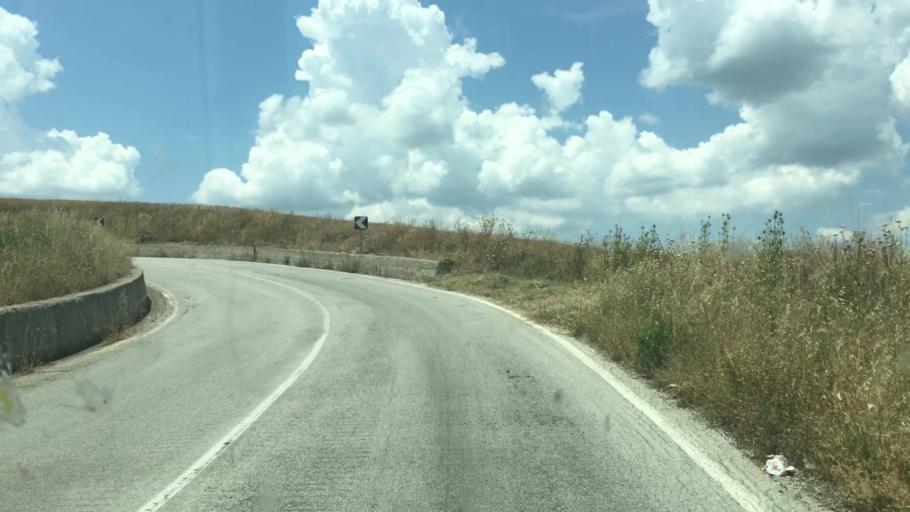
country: IT
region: Basilicate
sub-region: Provincia di Potenza
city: Tolve
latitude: 40.6897
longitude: 15.9849
